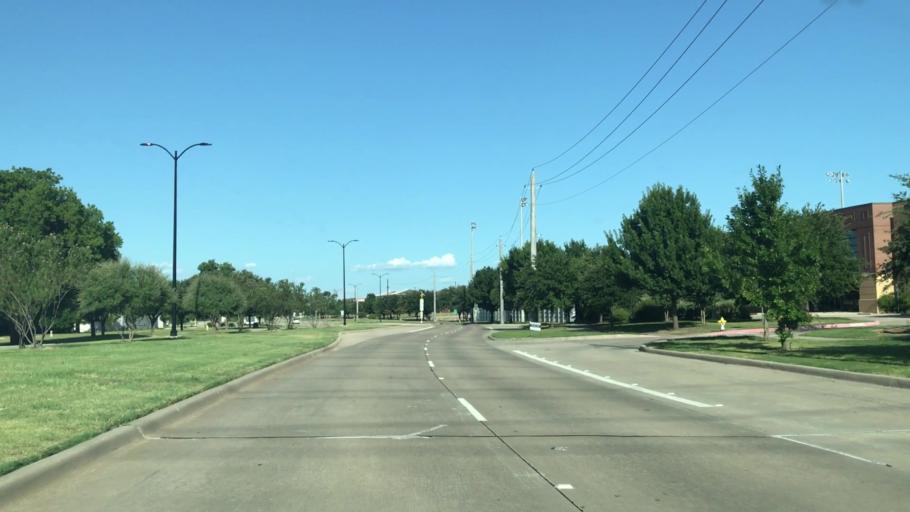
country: US
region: Texas
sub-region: Collin County
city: Frisco
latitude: 33.1379
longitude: -96.7745
